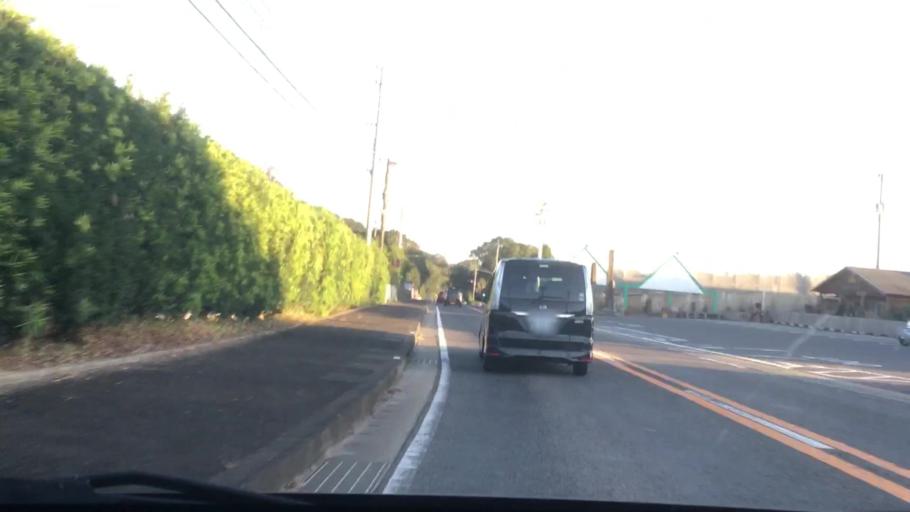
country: JP
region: Nagasaki
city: Sasebo
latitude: 33.0717
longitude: 129.7610
